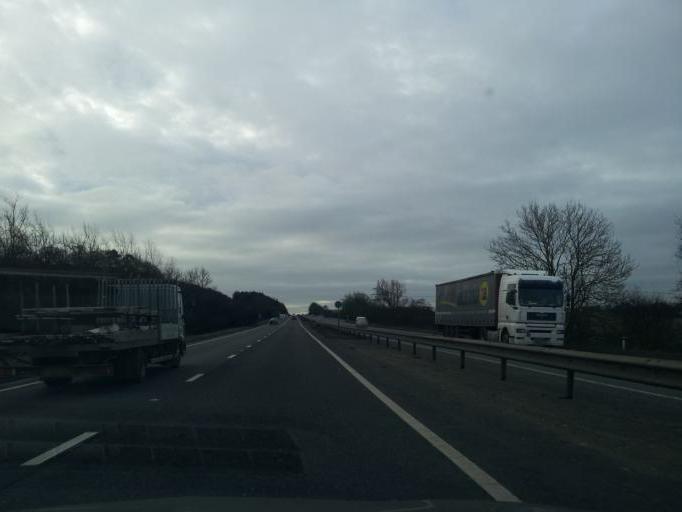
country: GB
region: England
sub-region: Lincolnshire
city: Barrowby
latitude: 52.9299
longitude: -0.6836
